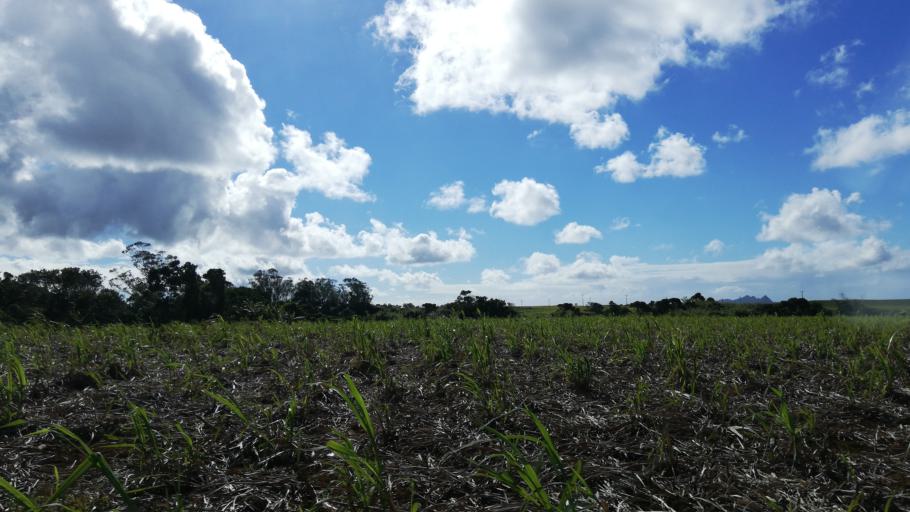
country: MU
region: Moka
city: Quartier Militaire
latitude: -20.2341
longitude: 57.5971
